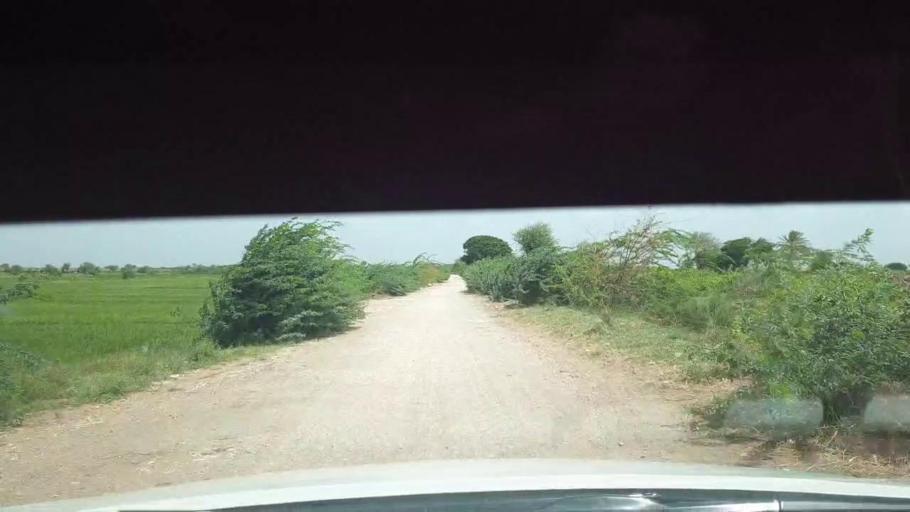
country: PK
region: Sindh
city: Kadhan
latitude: 24.5000
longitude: 68.9811
